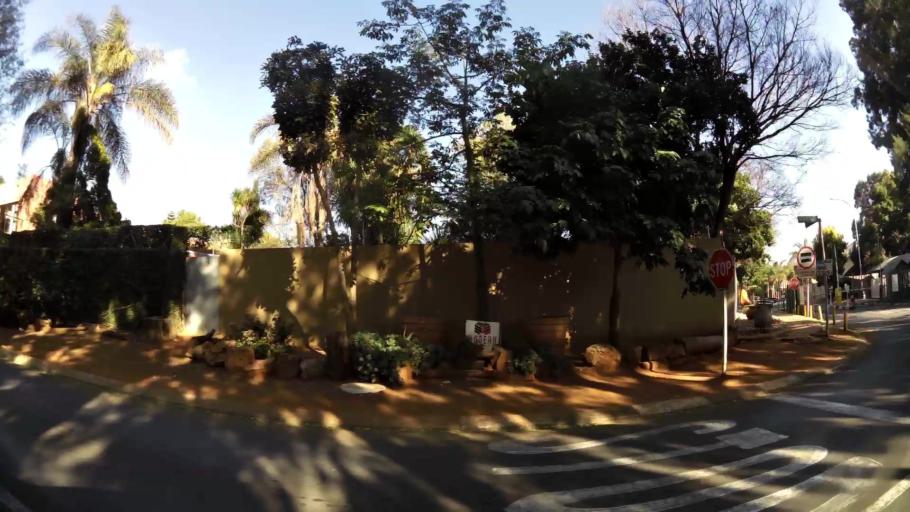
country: ZA
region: Gauteng
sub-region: City of Johannesburg Metropolitan Municipality
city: Modderfontein
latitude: -26.1618
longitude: 28.1429
